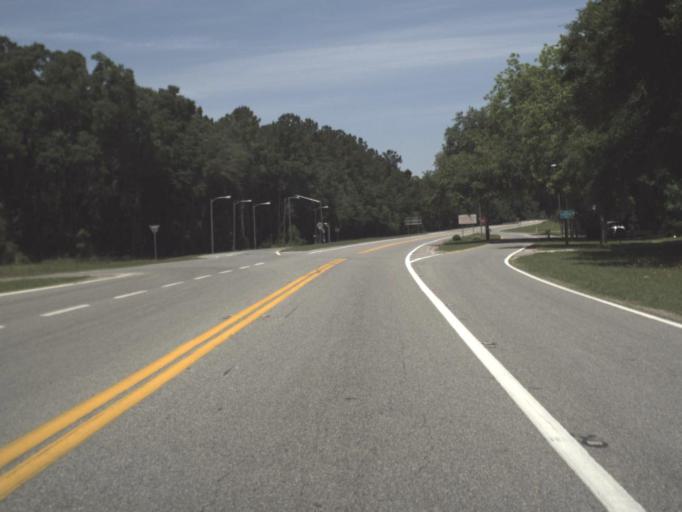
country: US
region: Florida
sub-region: Suwannee County
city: Live Oak
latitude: 30.3809
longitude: -83.1725
